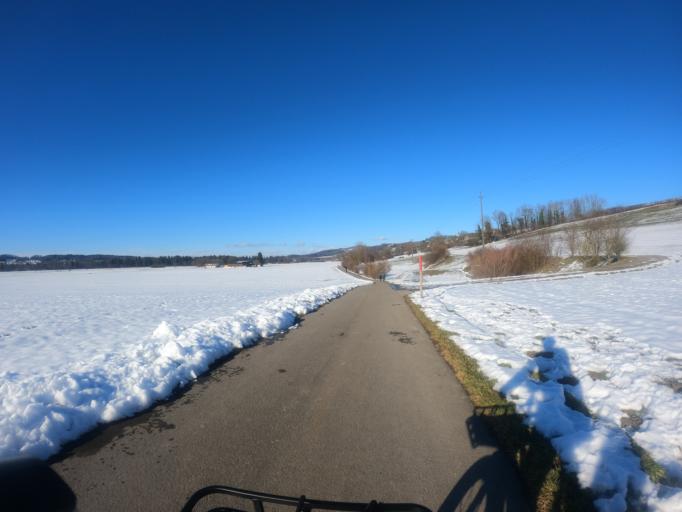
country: CH
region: Aargau
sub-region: Bezirk Bremgarten
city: Jonen
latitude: 47.3021
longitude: 8.3880
